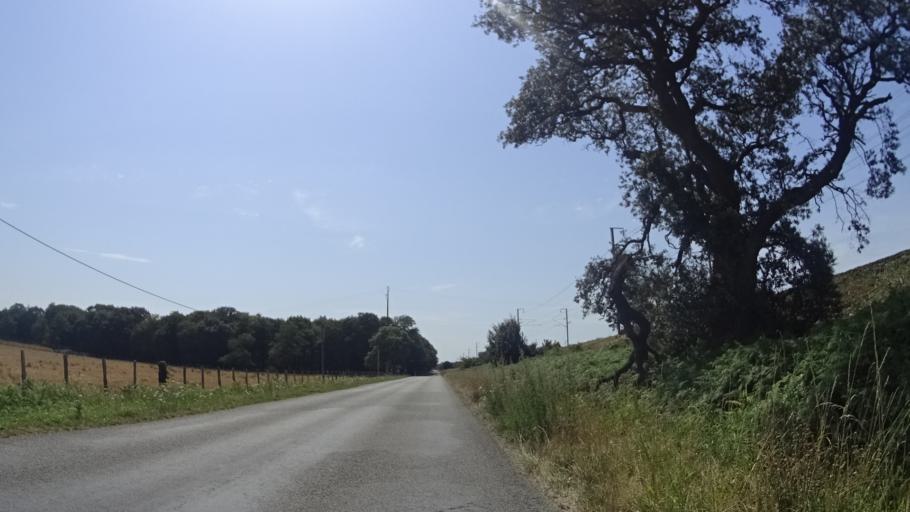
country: FR
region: Pays de la Loire
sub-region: Departement de la Loire-Atlantique
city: La Chapelle-Launay
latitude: 47.3563
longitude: -1.9849
